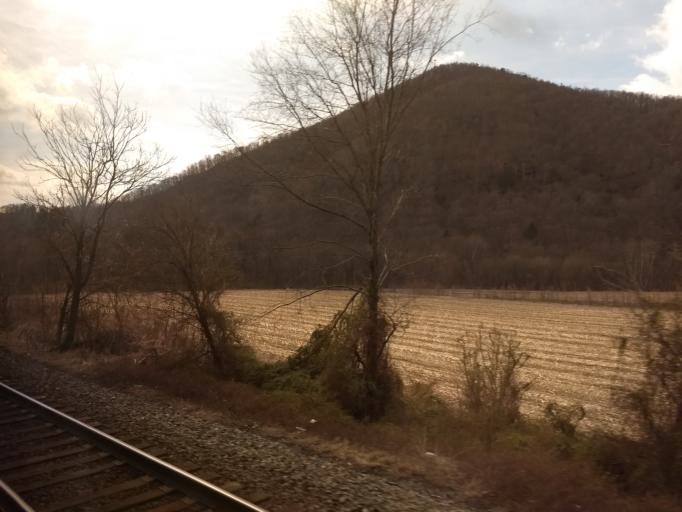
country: US
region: Pennsylvania
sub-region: Huntingdon County
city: Huntingdon
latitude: 40.4481
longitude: -77.9610
